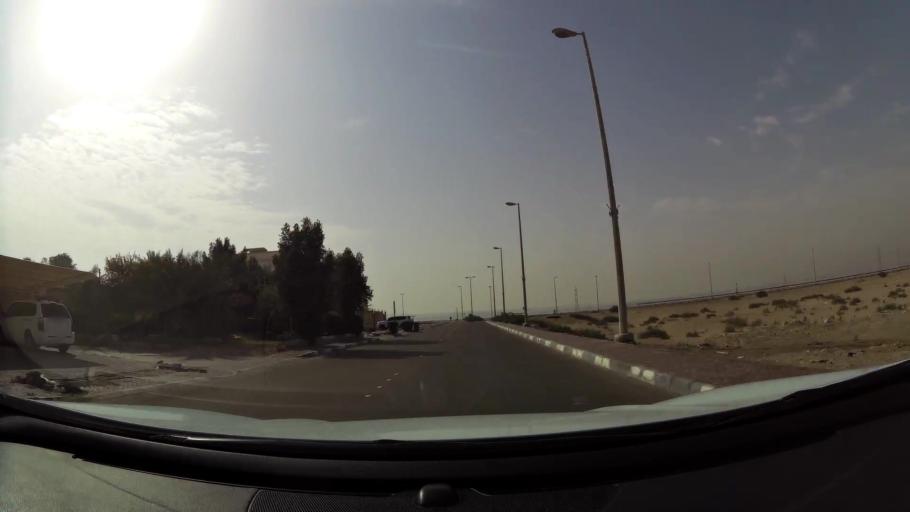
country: AE
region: Abu Dhabi
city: Abu Dhabi
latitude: 24.2634
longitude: 54.6946
